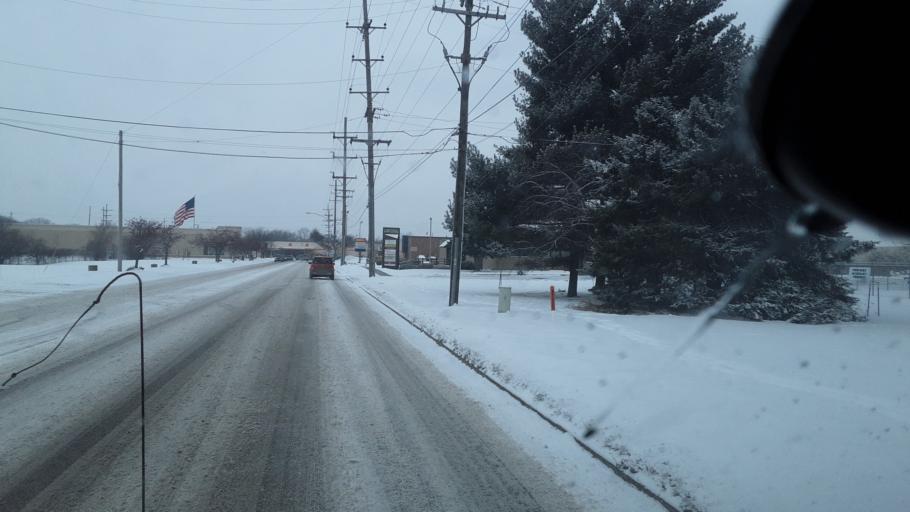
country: US
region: Michigan
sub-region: Jackson County
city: Jackson
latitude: 42.2653
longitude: -84.4251
